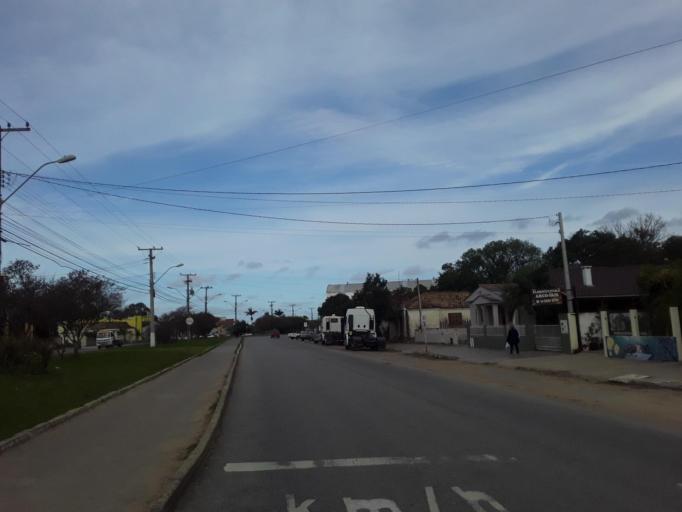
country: BR
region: Rio Grande do Sul
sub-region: Sao Lourenco Do Sul
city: Sao Lourenco do Sul
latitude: -31.3518
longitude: -51.9901
